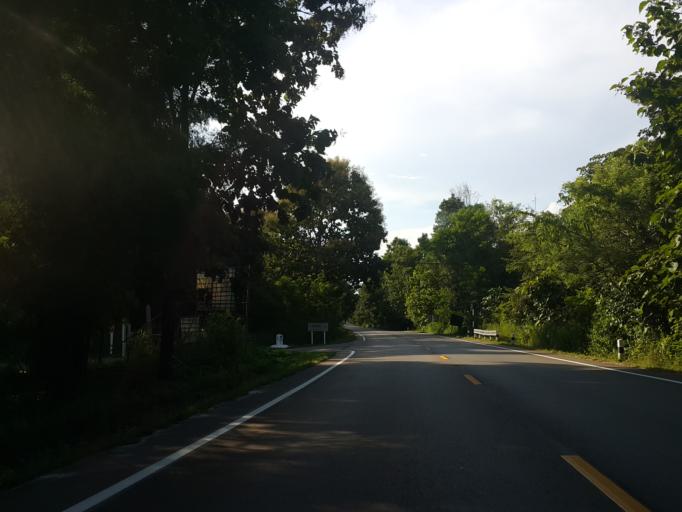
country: TH
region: Chiang Mai
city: Mae Taeng
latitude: 19.0825
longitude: 99.1018
